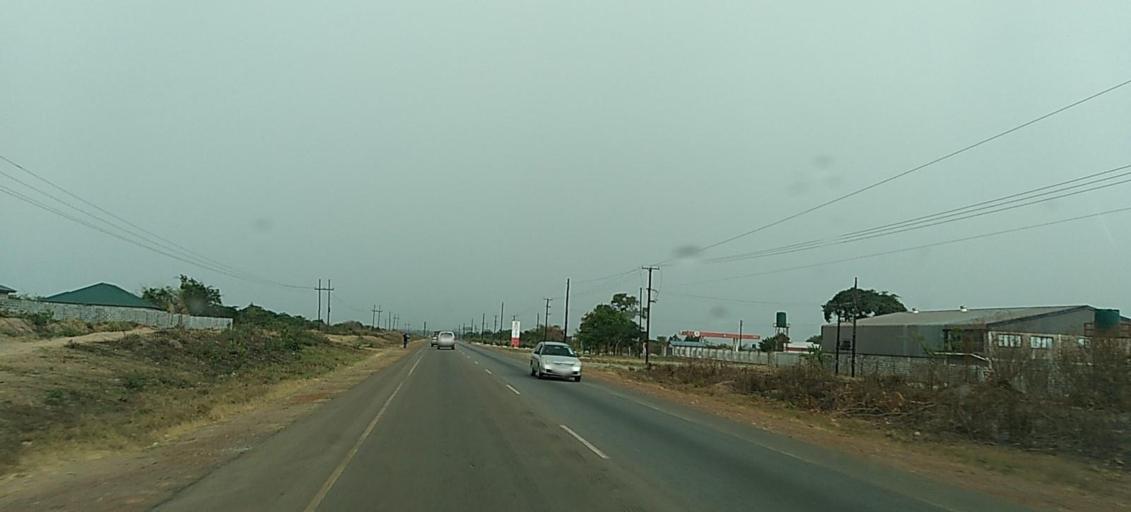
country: ZM
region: Copperbelt
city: Kalulushi
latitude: -12.8354
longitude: 28.1240
